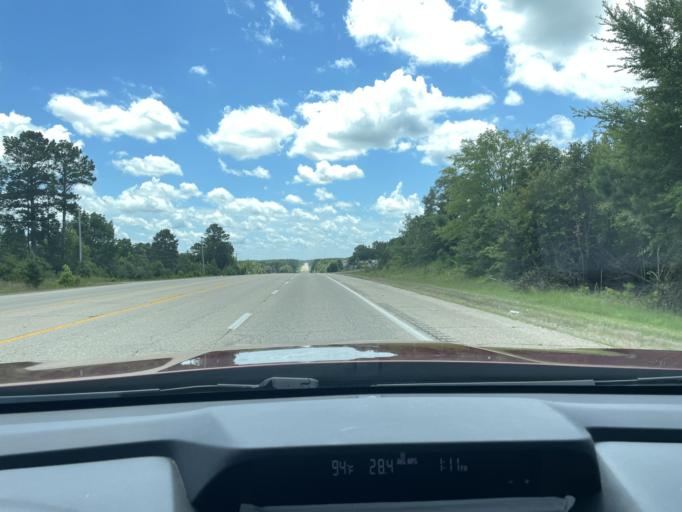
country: US
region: Arkansas
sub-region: Drew County
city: Monticello
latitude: 33.7059
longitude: -91.8077
